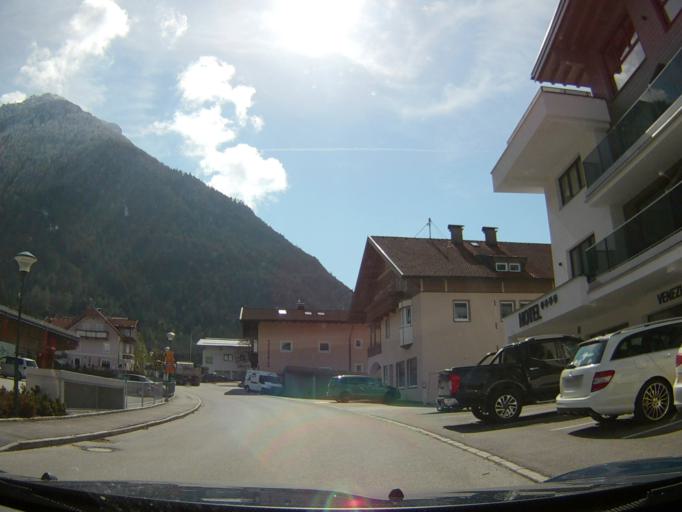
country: AT
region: Tyrol
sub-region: Politischer Bezirk Schwaz
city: Jenbach
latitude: 47.4226
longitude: 11.7504
